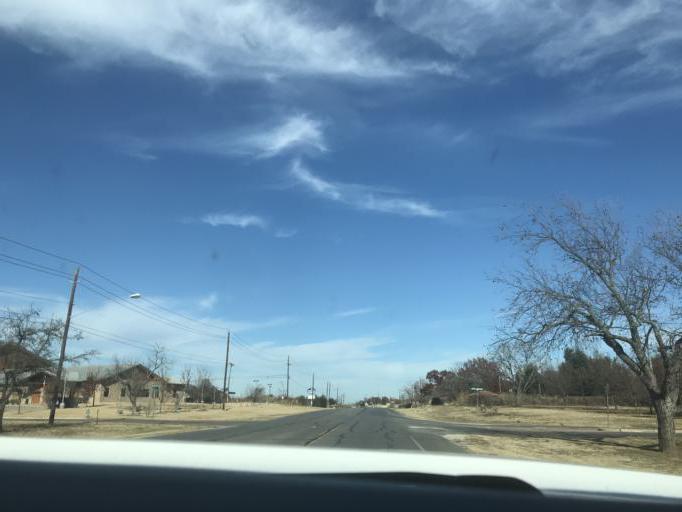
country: US
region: Texas
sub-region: Erath County
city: Stephenville
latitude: 32.2134
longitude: -98.2441
